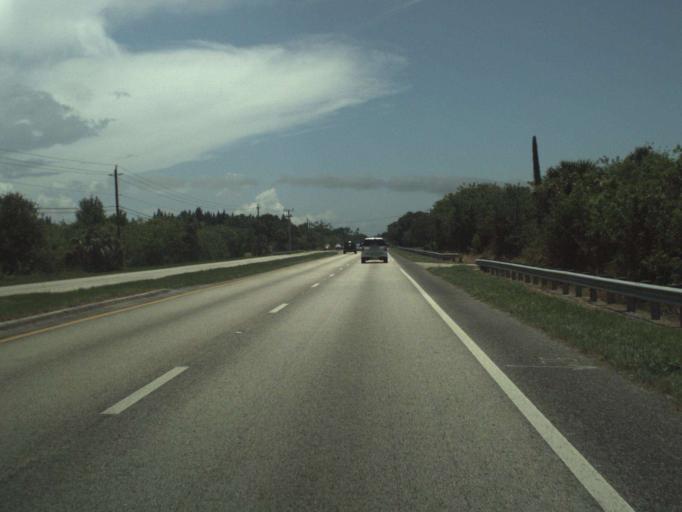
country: US
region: Florida
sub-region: Indian River County
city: Winter Beach
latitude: 27.7363
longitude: -80.4283
